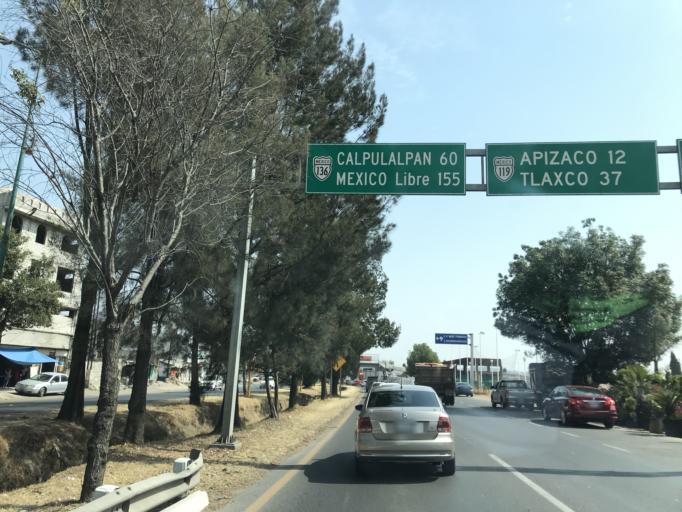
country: MX
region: Tlaxcala
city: Tlaxcala de Xicohtencatl
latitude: 19.3224
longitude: -98.2009
